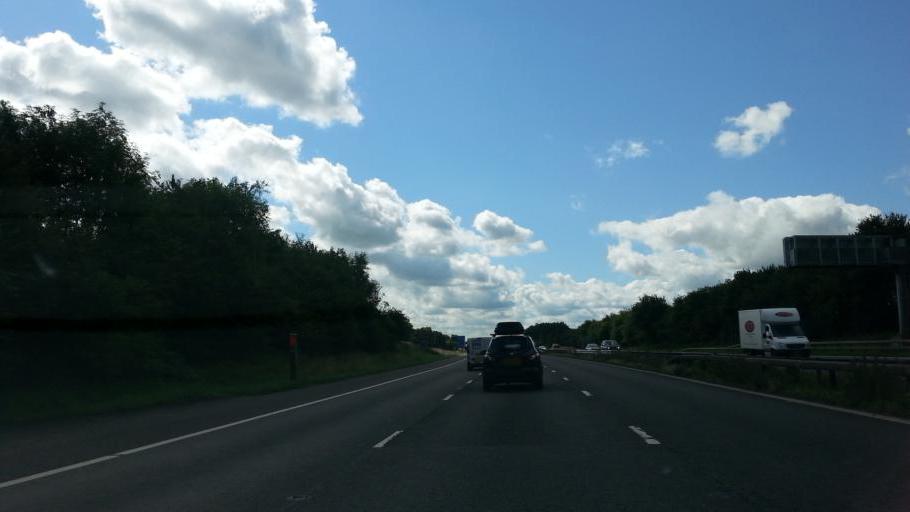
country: GB
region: England
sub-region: Leicestershire
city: Markfield
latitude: 52.7093
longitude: -1.2915
